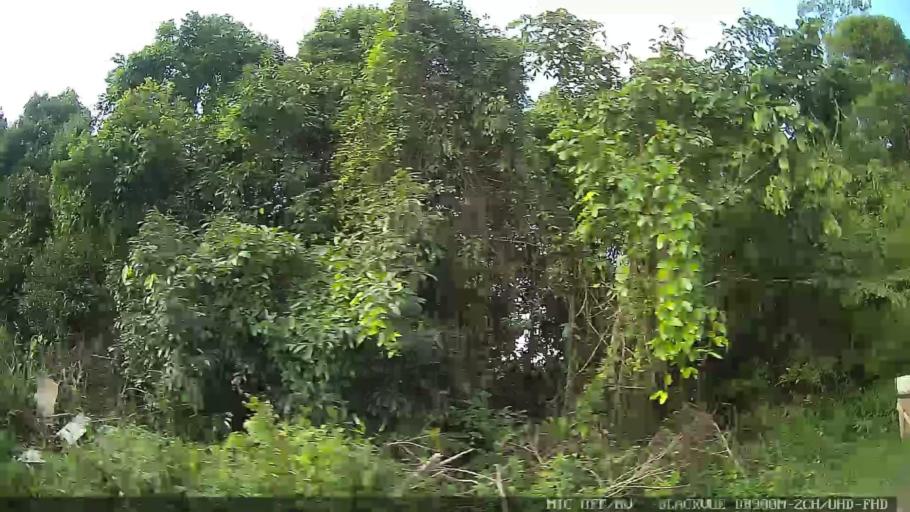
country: BR
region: Sao Paulo
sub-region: Itanhaem
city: Itanhaem
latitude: -24.1712
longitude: -46.8393
